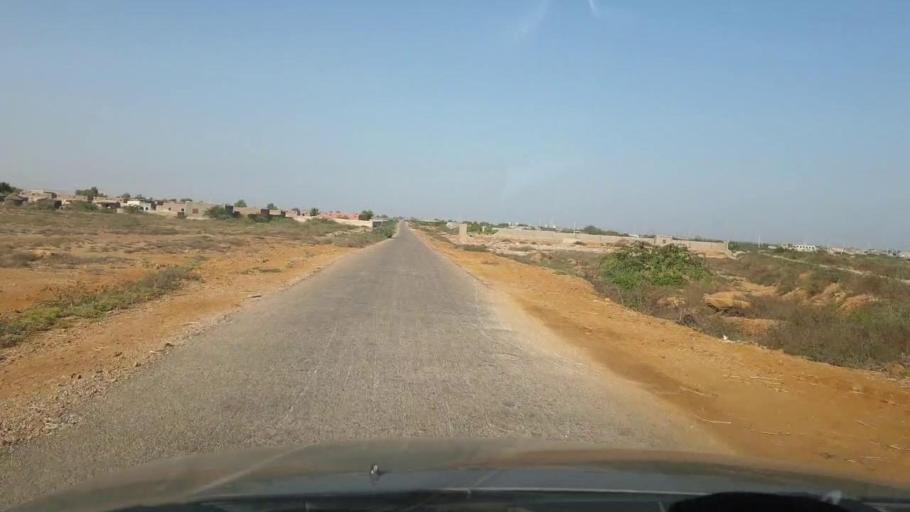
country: PK
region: Sindh
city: Bulri
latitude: 25.0965
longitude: 68.2356
